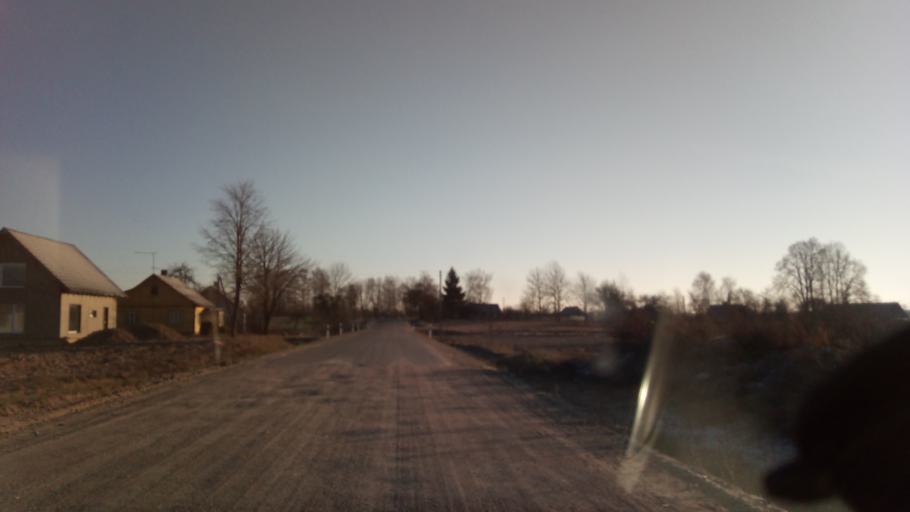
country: LT
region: Alytaus apskritis
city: Druskininkai
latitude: 54.1396
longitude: 23.9648
